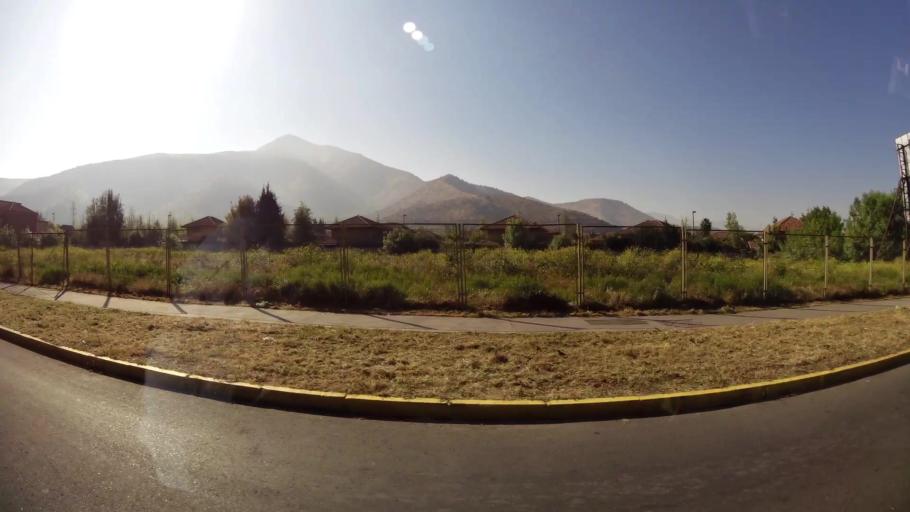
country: CL
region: Santiago Metropolitan
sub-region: Provincia de Chacabuco
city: Chicureo Abajo
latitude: -33.3454
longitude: -70.6699
